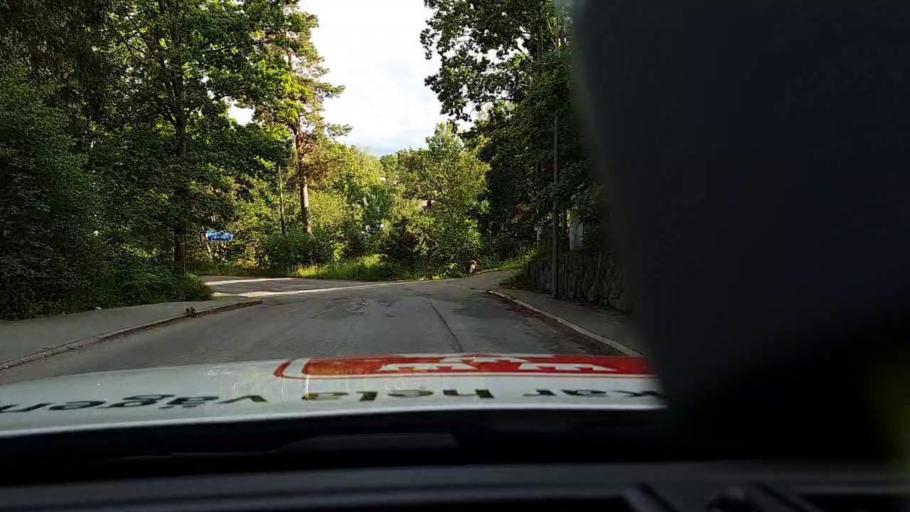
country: SE
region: Stockholm
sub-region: Huddinge Kommun
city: Huddinge
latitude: 59.2626
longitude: 17.9861
